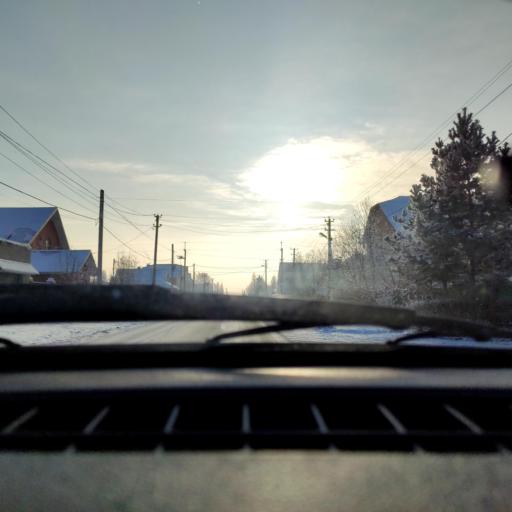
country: RU
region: Bashkortostan
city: Ufa
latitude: 54.5998
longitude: 55.9355
